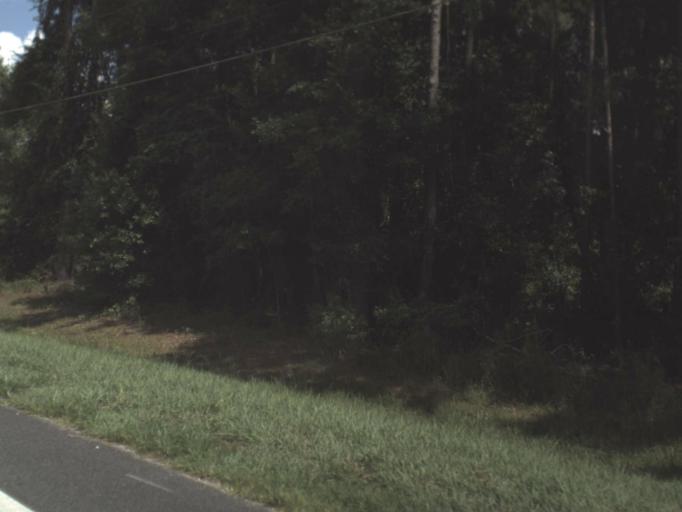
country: US
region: Florida
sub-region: Alachua County
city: Gainesville
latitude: 29.6736
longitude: -82.2583
